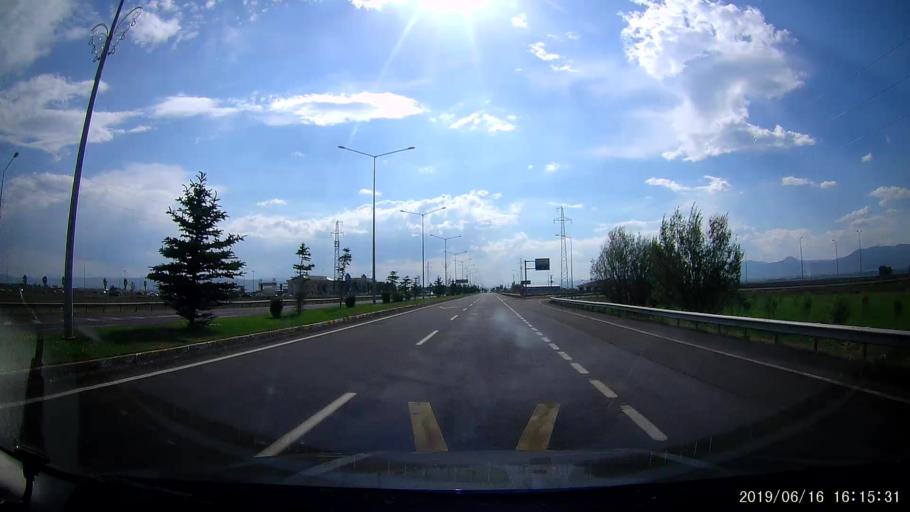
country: TR
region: Erzurum
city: Erzurum
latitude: 39.9620
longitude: 41.2246
